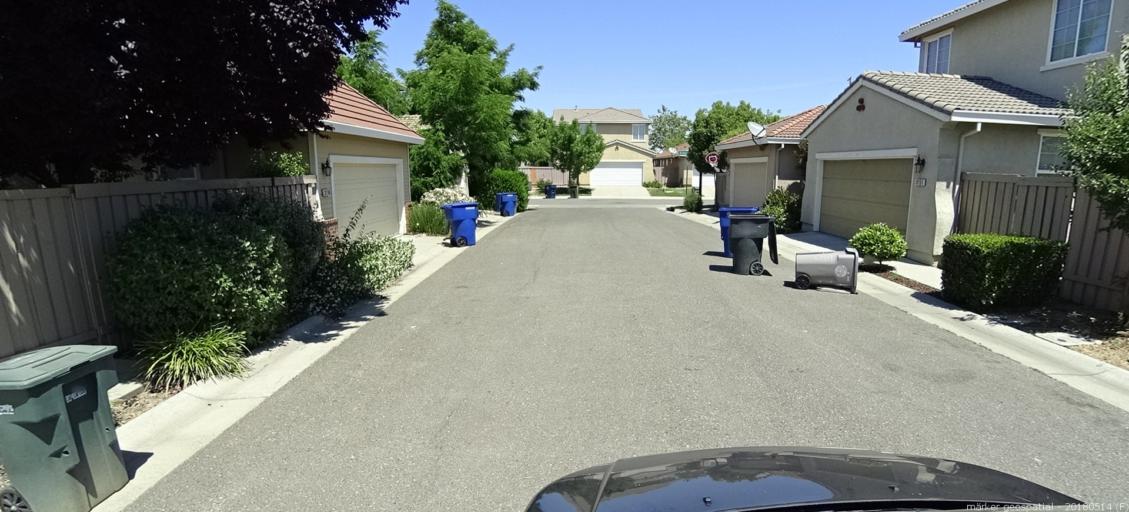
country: US
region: California
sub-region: Yolo County
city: West Sacramento
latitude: 38.6270
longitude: -121.5211
